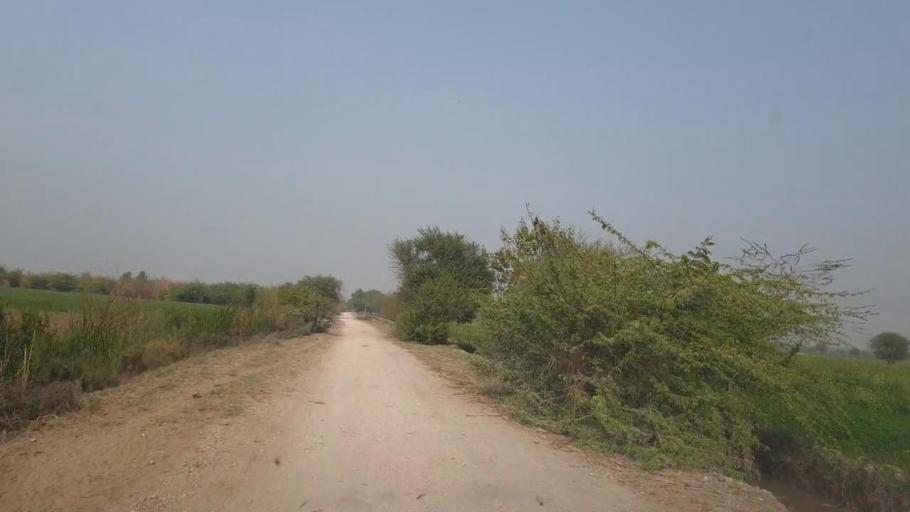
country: PK
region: Sindh
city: Mirpur Khas
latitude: 25.5601
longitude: 69.1340
